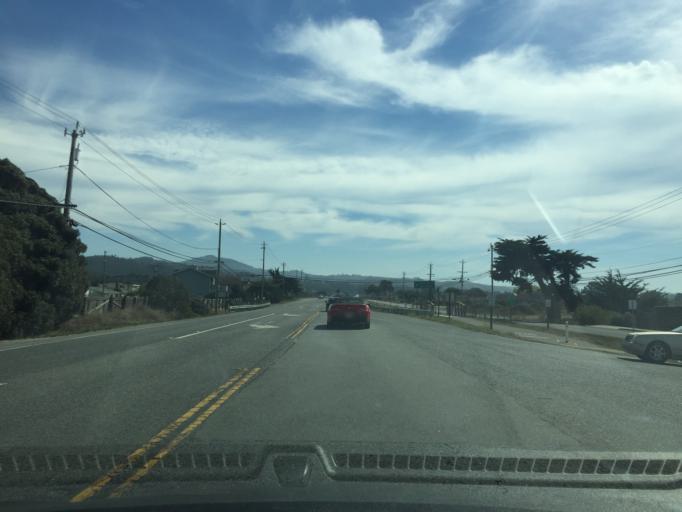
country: US
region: California
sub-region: San Mateo County
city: Half Moon Bay
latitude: 37.4766
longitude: -122.4398
